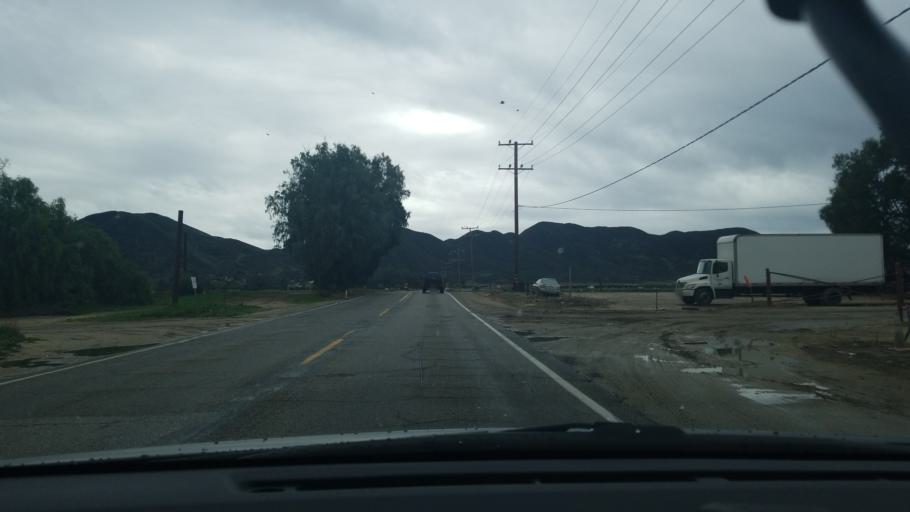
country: US
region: California
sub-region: Riverside County
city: Green Acres
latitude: 33.7128
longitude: -117.0326
